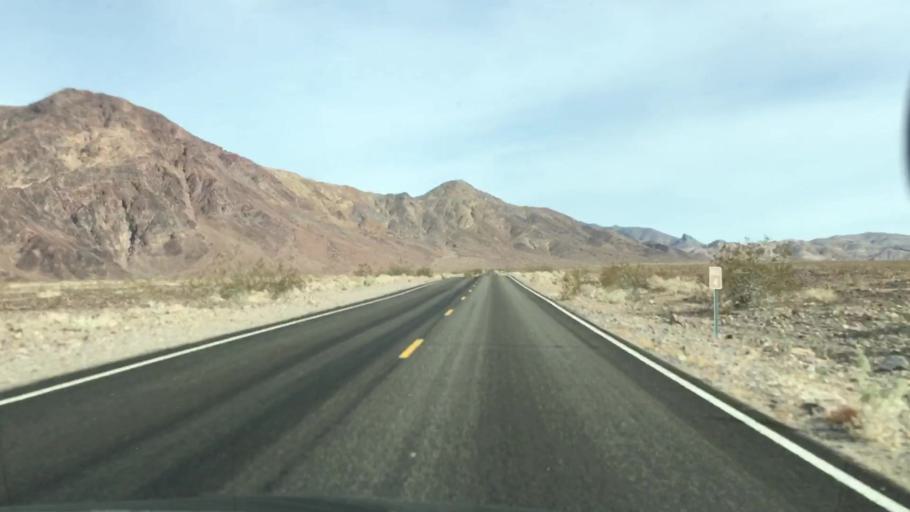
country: US
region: Nevada
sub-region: Nye County
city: Beatty
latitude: 36.6912
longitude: -117.0031
